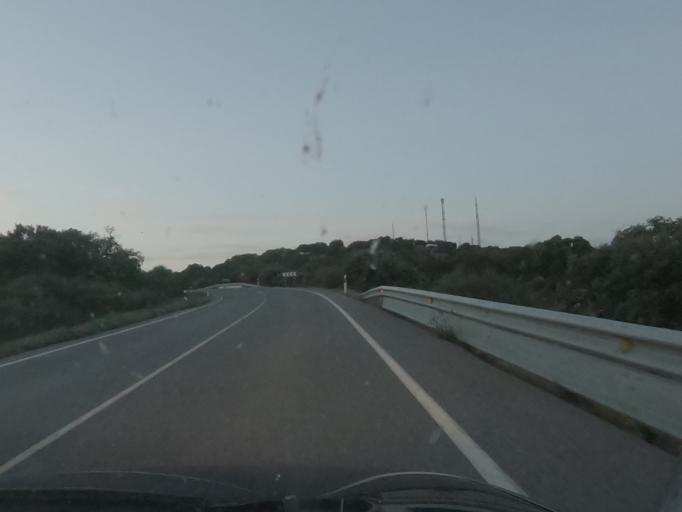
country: ES
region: Extremadura
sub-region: Provincia de Caceres
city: Alcantara
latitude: 39.7444
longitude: -6.9016
